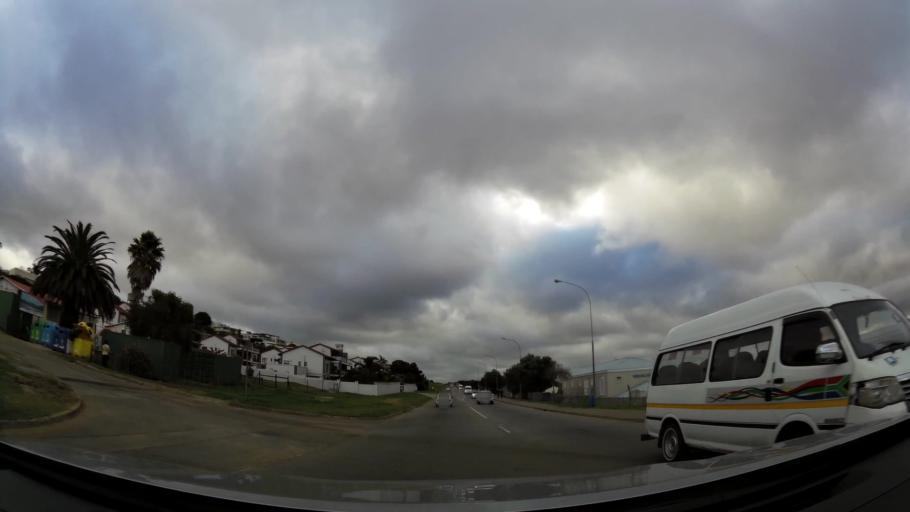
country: ZA
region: Western Cape
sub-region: Eden District Municipality
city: Plettenberg Bay
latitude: -34.0536
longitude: 23.3651
